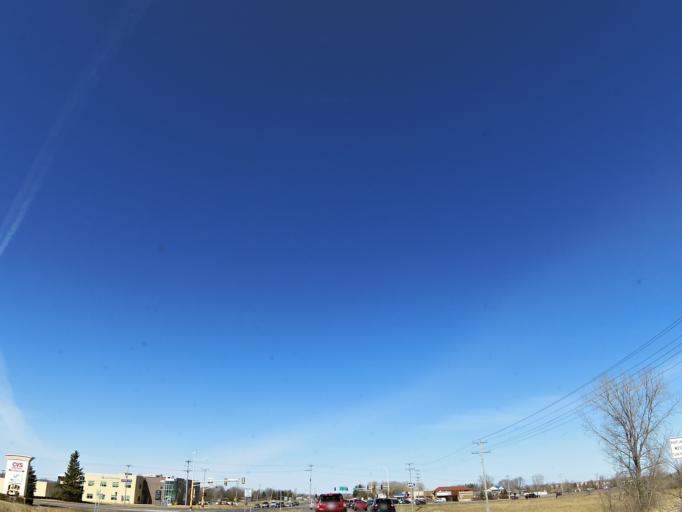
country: US
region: Minnesota
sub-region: Hennepin County
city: Plymouth
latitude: 45.0312
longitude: -93.5059
